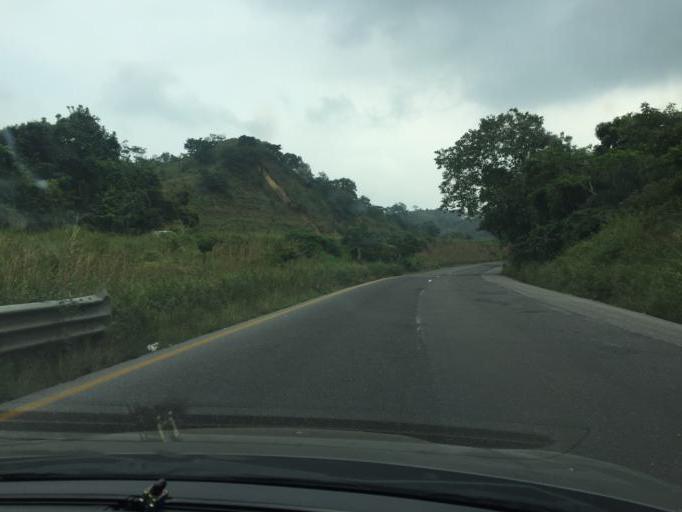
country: MX
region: Veracruz
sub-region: Moloacan
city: Tlacuilolapan
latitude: 18.0761
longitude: -94.2691
